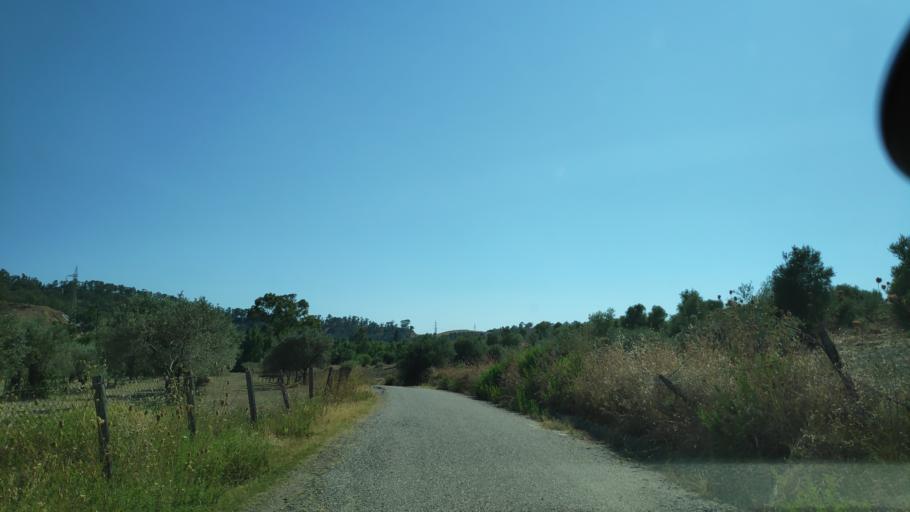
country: IT
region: Calabria
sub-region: Provincia di Reggio Calabria
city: Monasterace
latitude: 38.4301
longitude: 16.5245
